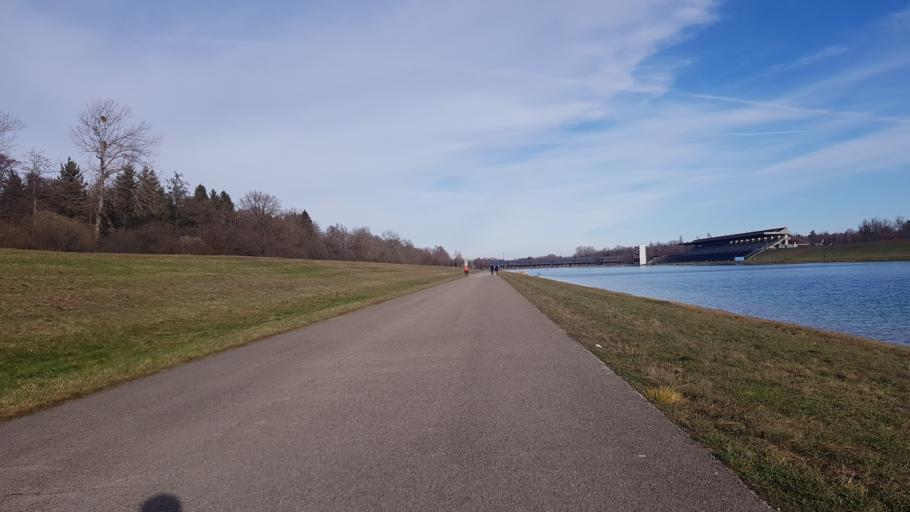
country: DE
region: Bavaria
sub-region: Upper Bavaria
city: Oberschleissheim
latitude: 48.2445
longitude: 11.5160
